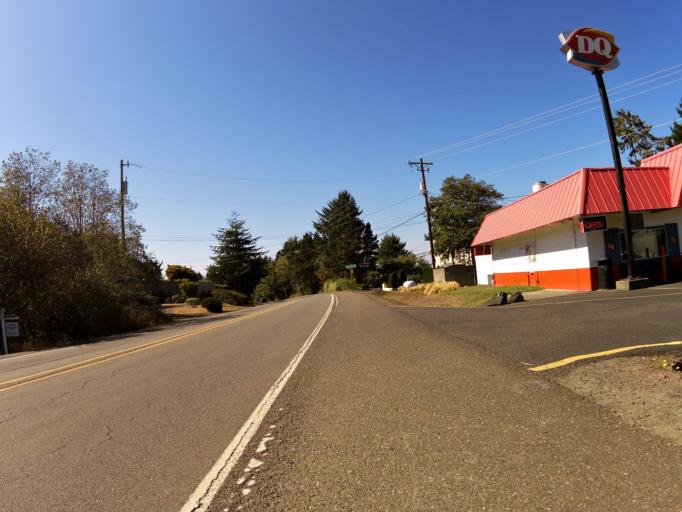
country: US
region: Oregon
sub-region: Coos County
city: Barview
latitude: 43.3595
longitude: -124.3060
